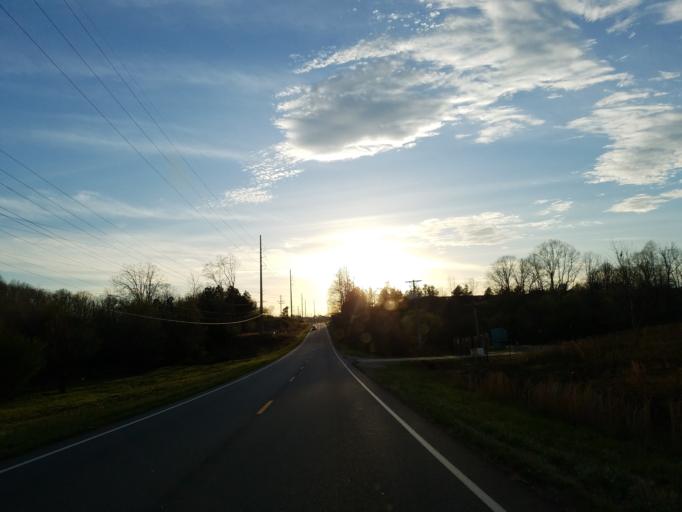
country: US
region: Georgia
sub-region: Dawson County
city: Dawsonville
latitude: 34.3538
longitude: -84.0368
